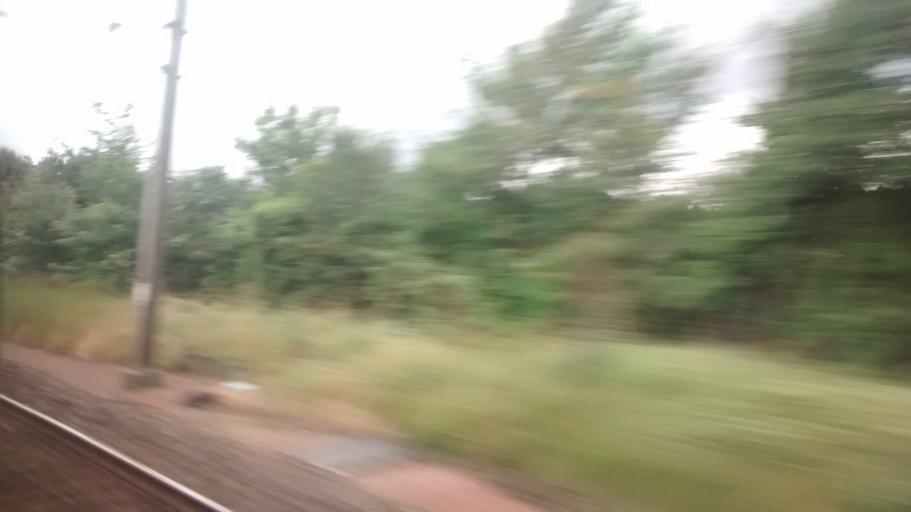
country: FR
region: Pays de la Loire
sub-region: Departement de la Sarthe
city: Champagne
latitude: 48.0117
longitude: 0.3077
